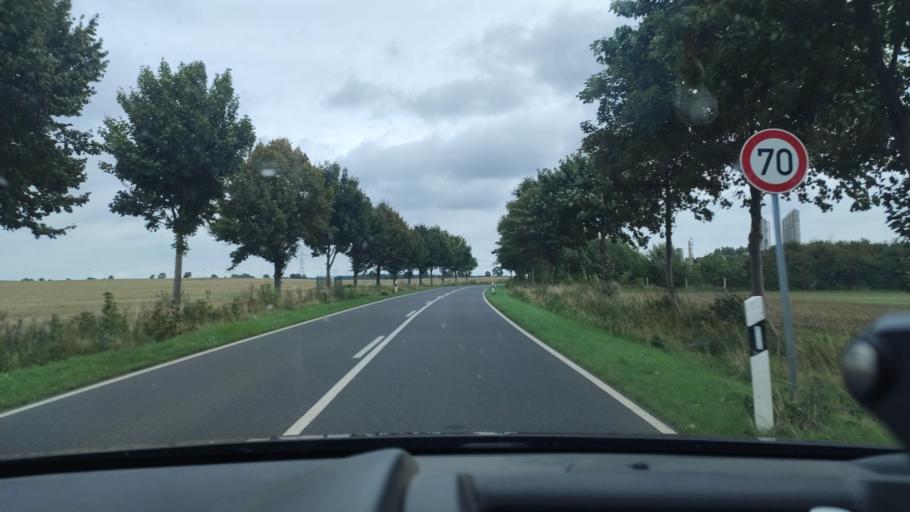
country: DE
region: Mecklenburg-Vorpommern
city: Guestrow
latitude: 53.8273
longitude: 12.1904
